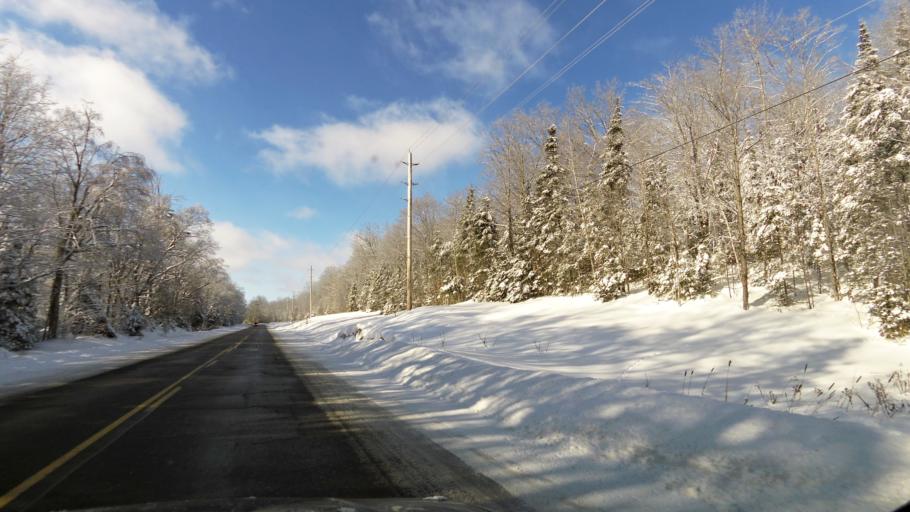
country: CA
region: Ontario
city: Bancroft
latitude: 45.0120
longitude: -78.3307
